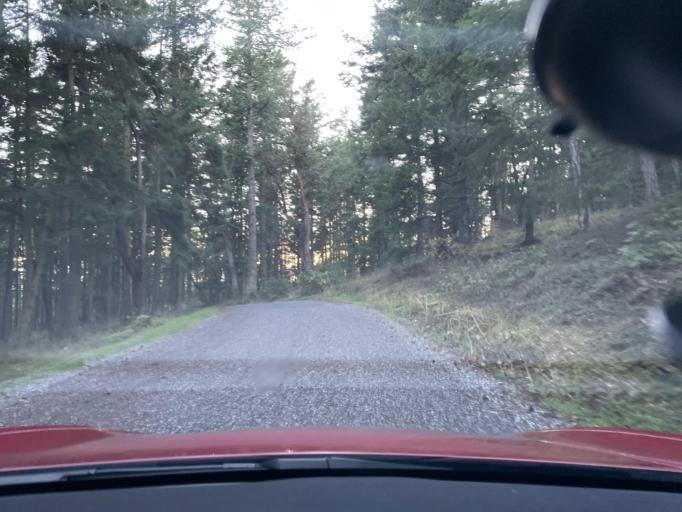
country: US
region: Washington
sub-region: San Juan County
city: Friday Harbor
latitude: 48.6133
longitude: -123.1481
